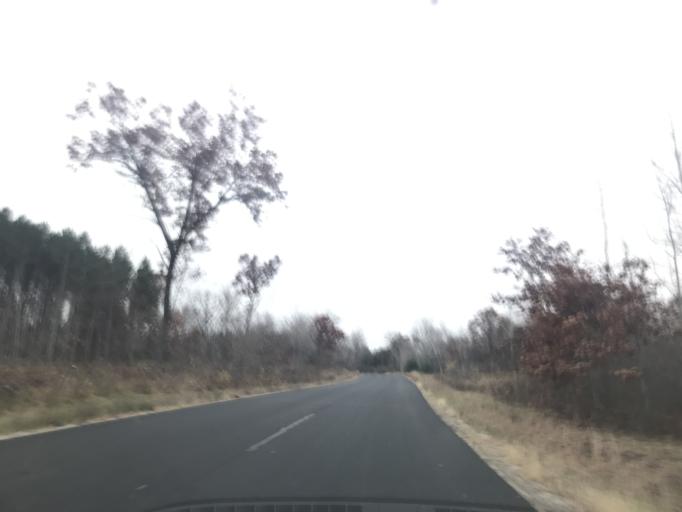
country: US
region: Wisconsin
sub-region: Marinette County
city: Peshtigo
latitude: 45.1292
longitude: -87.7506
